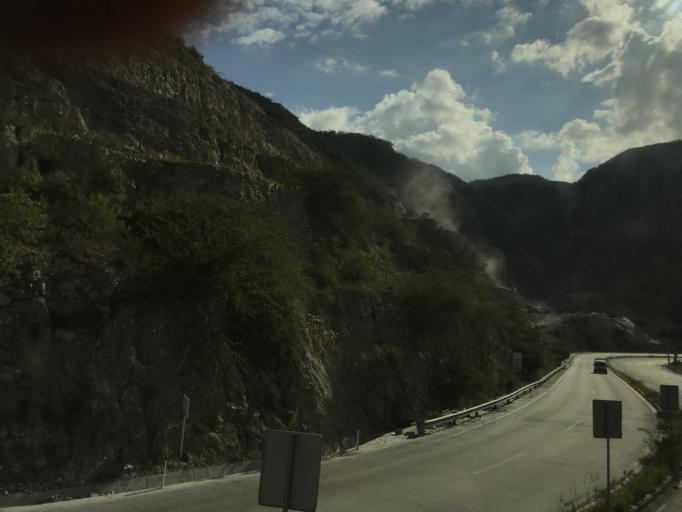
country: GT
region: El Progreso
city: Guastatoya
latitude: 14.8482
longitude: -90.1148
